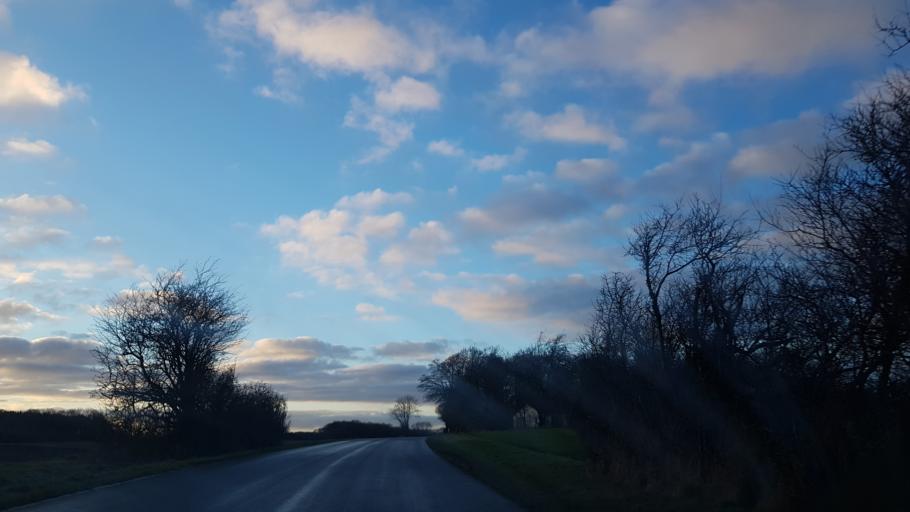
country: DK
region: South Denmark
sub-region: Kolding Kommune
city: Vamdrup
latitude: 55.3631
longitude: 9.3309
